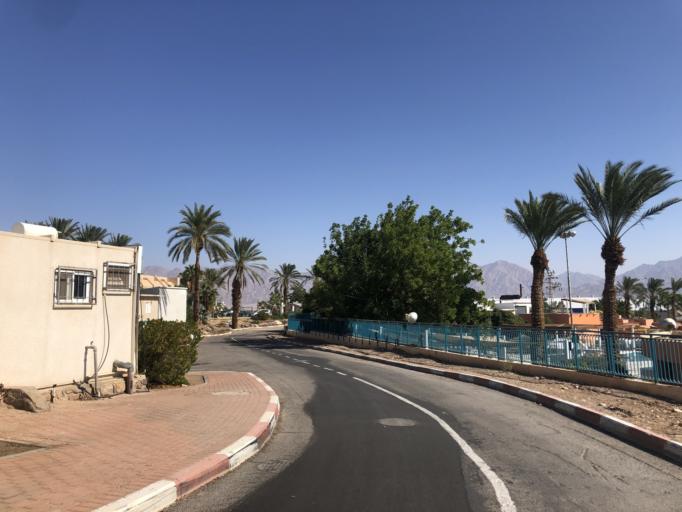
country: IL
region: Southern District
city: Eilat
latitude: 29.5810
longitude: 34.9623
